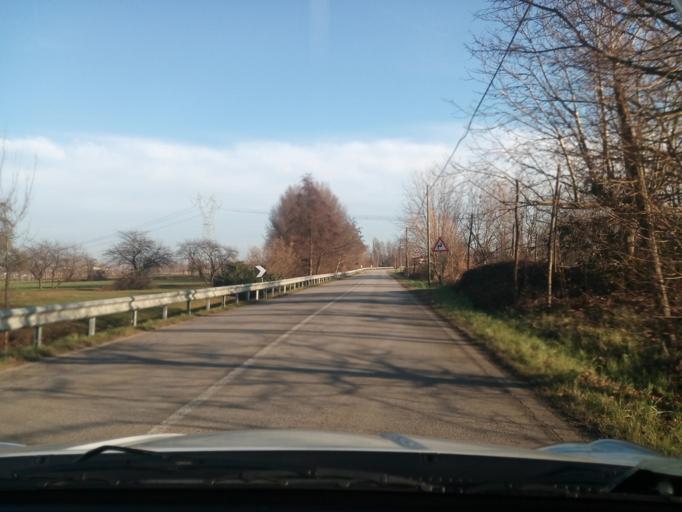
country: IT
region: Veneto
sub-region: Provincia di Vicenza
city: Novoledo
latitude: 45.6444
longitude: 11.5216
